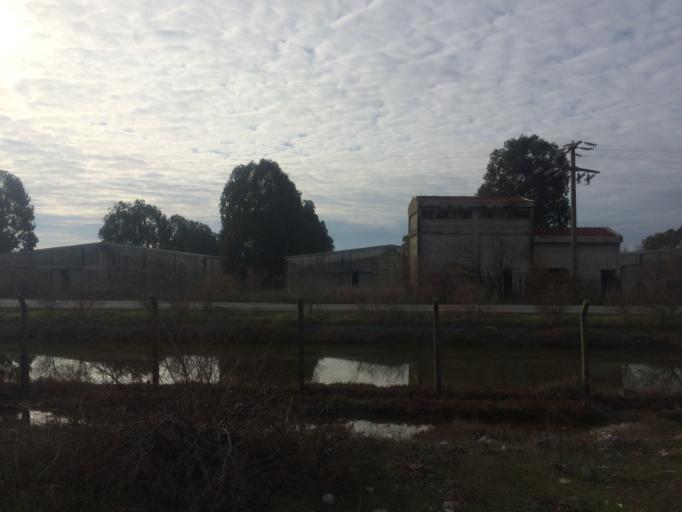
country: TR
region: Izmir
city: Menemen
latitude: 38.4938
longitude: 26.9436
